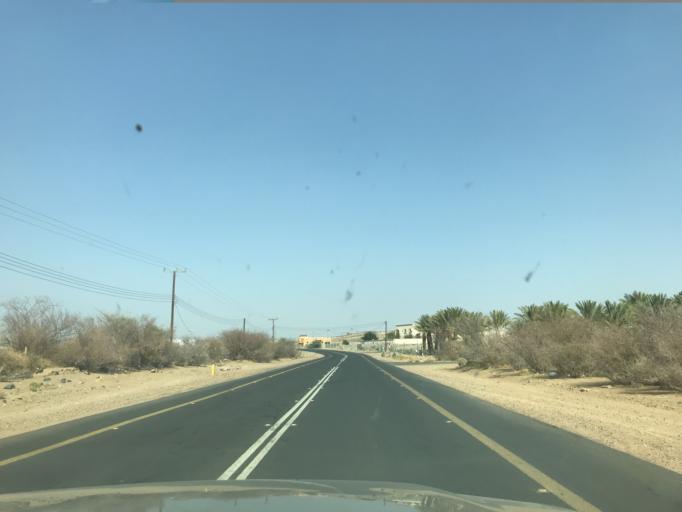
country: SA
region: Mintaqat al Bahah
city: Al Bahah
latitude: 20.4352
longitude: 41.9127
